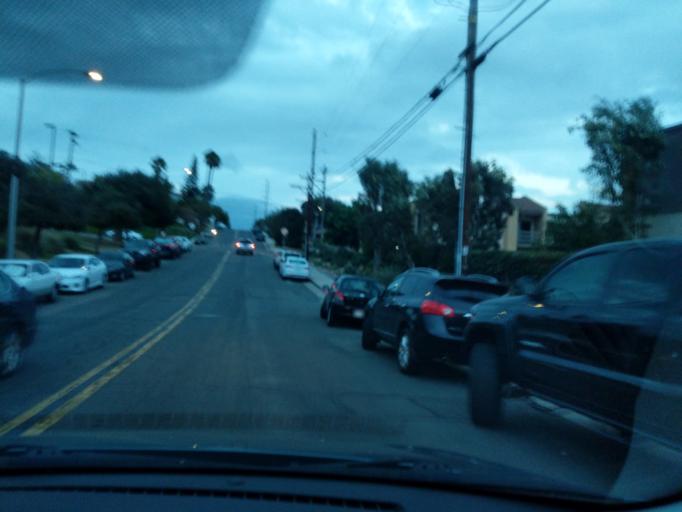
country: US
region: California
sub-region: San Diego County
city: San Diego
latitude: 32.7170
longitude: -117.1240
